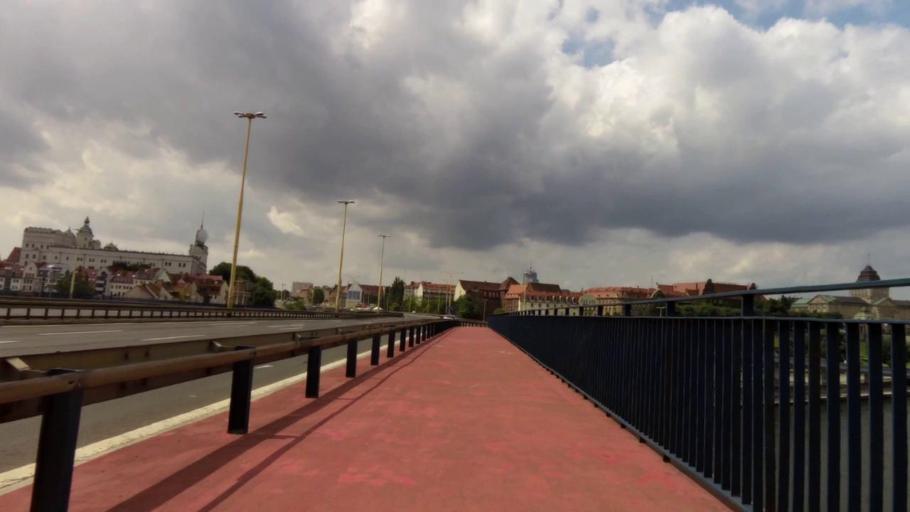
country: PL
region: West Pomeranian Voivodeship
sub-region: Szczecin
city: Szczecin
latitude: 53.4256
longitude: 14.5665
